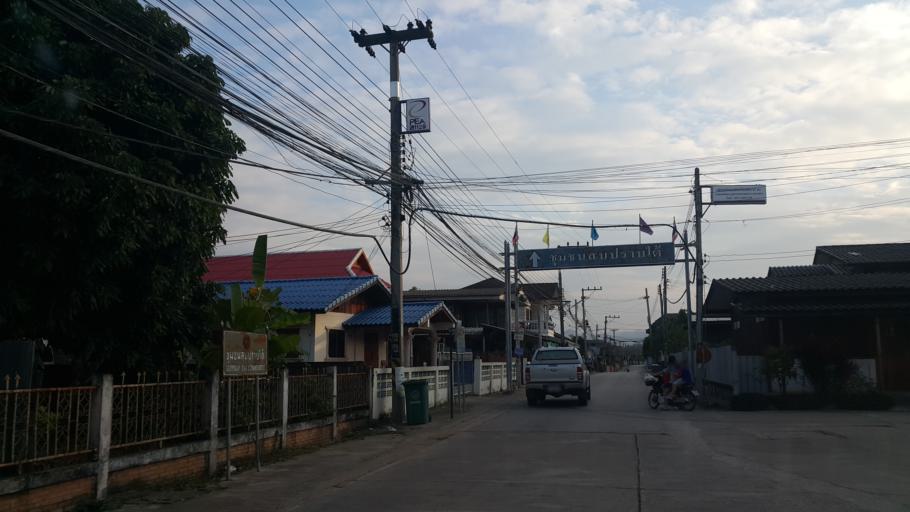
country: TH
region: Lampang
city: Sop Prap
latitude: 17.8803
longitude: 99.3335
